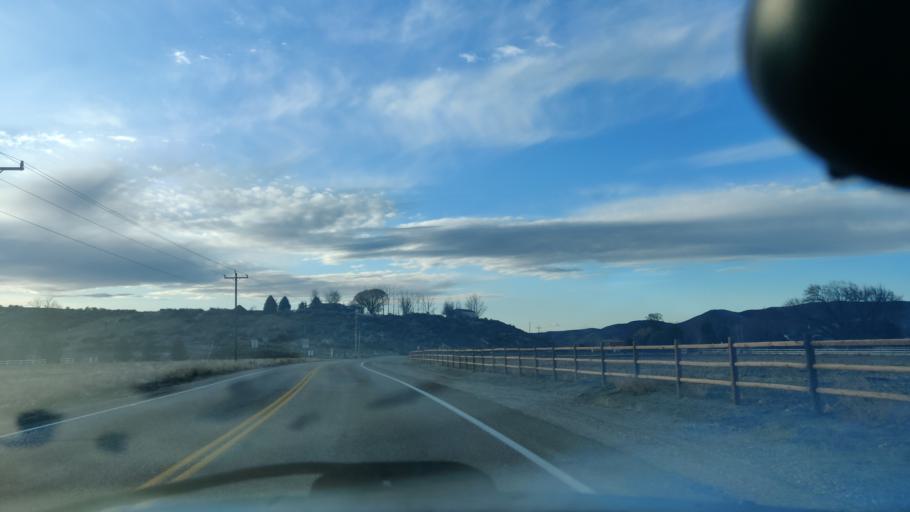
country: US
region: Idaho
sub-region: Ada County
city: Eagle
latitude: 43.7300
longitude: -116.2665
